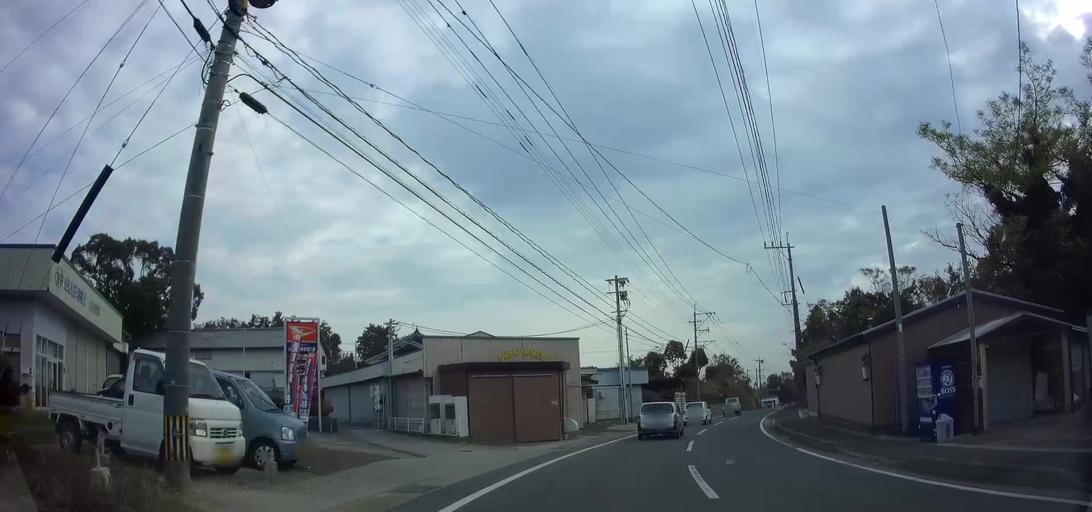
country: JP
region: Nagasaki
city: Shimabara
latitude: 32.6921
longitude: 130.3090
